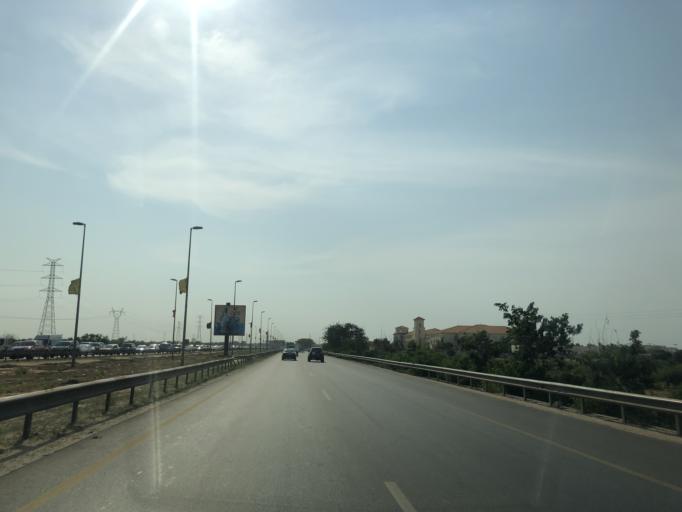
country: AO
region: Luanda
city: Luanda
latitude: -8.9739
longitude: 13.2739
